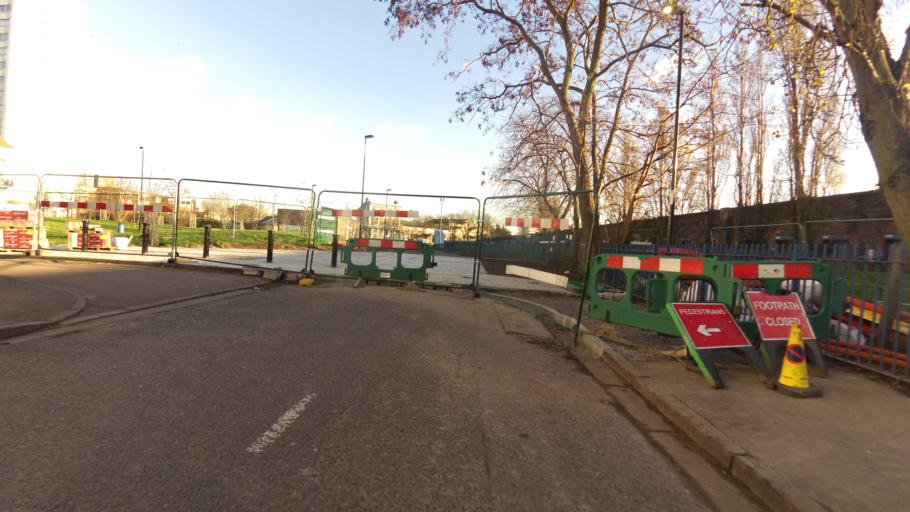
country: GB
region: England
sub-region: Greater London
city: Poplar
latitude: 51.4815
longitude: -0.0327
